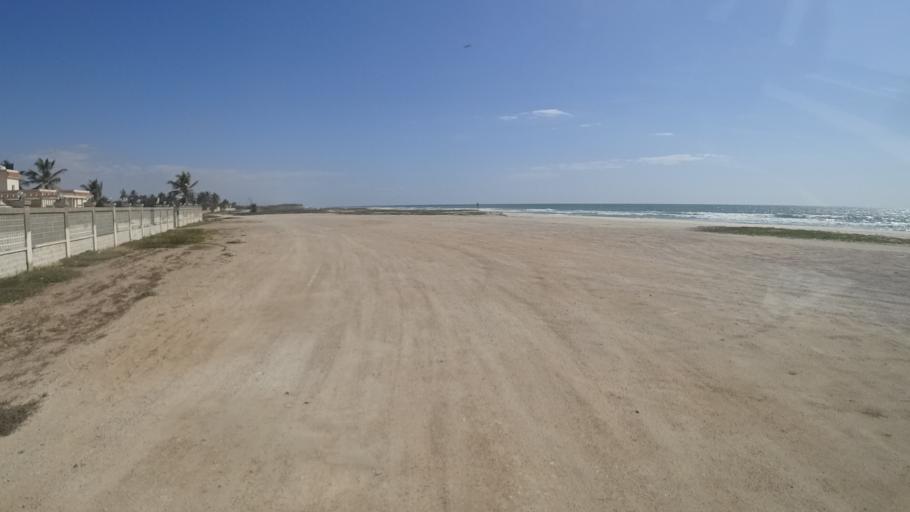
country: OM
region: Zufar
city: Salalah
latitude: 16.9932
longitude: 54.0561
